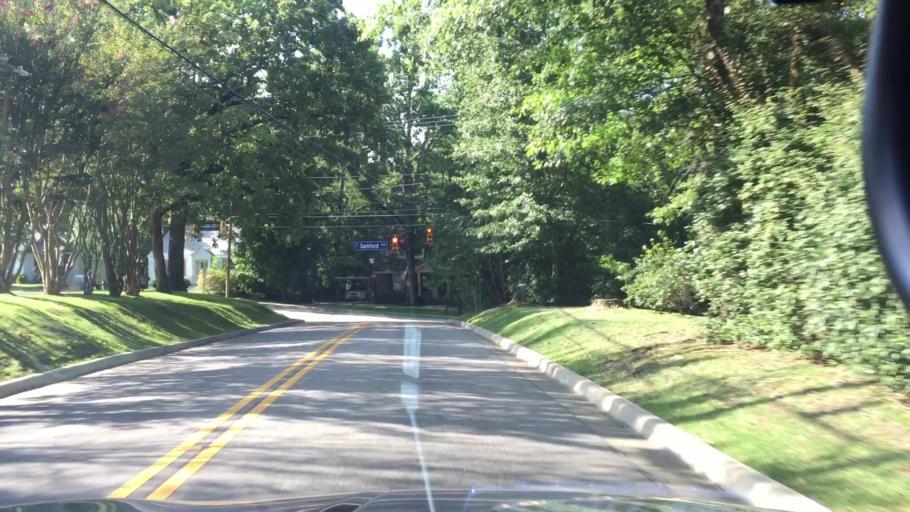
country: US
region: Alabama
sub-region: Lee County
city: Auburn
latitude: 32.5983
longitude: -85.4742
